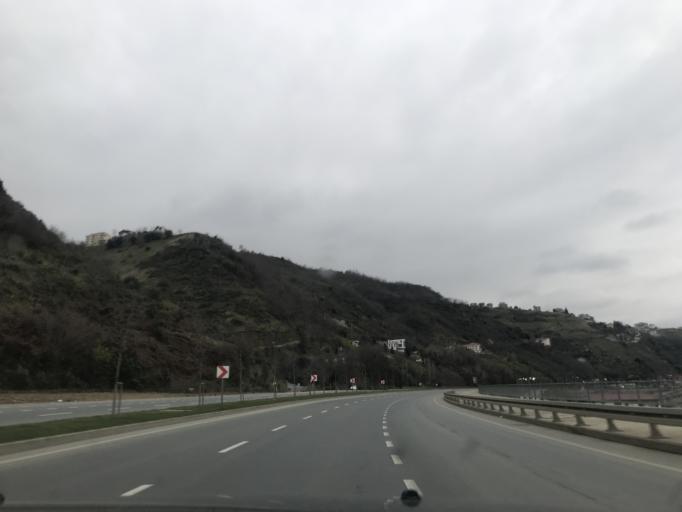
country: TR
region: Trabzon
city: Trabzon
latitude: 40.9954
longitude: 39.6524
